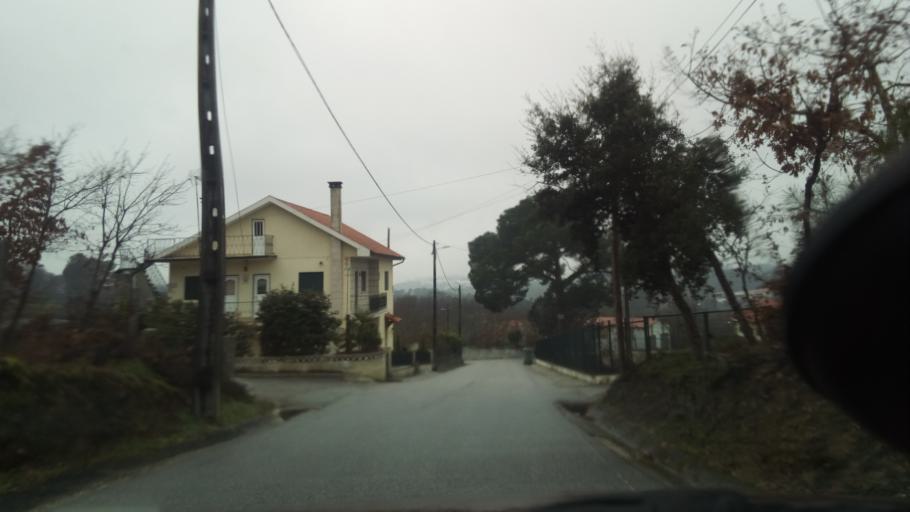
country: PT
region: Viseu
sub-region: Mangualde
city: Mangualde
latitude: 40.6144
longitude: -7.7786
